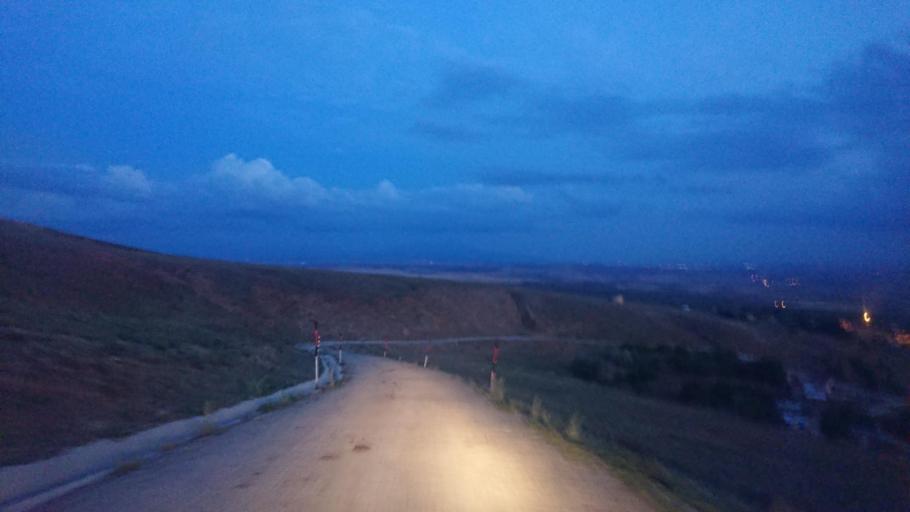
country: TR
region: Aksaray
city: Ortakoy
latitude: 38.6373
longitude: 34.0173
